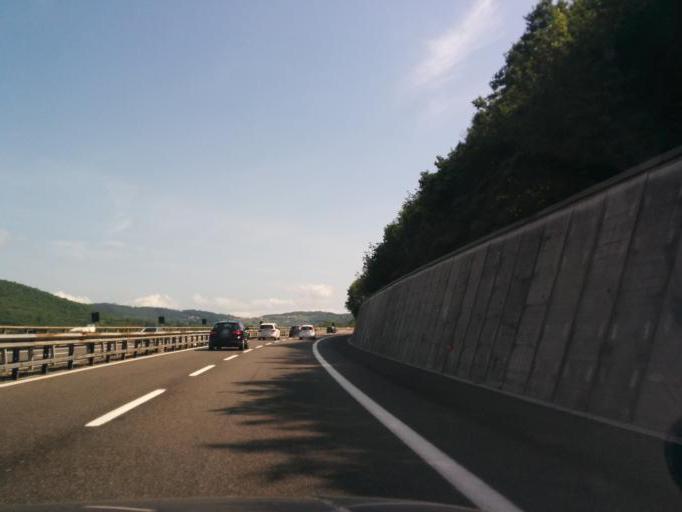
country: IT
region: Tuscany
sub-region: Province of Florence
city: Carraia
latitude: 43.9107
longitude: 11.1953
